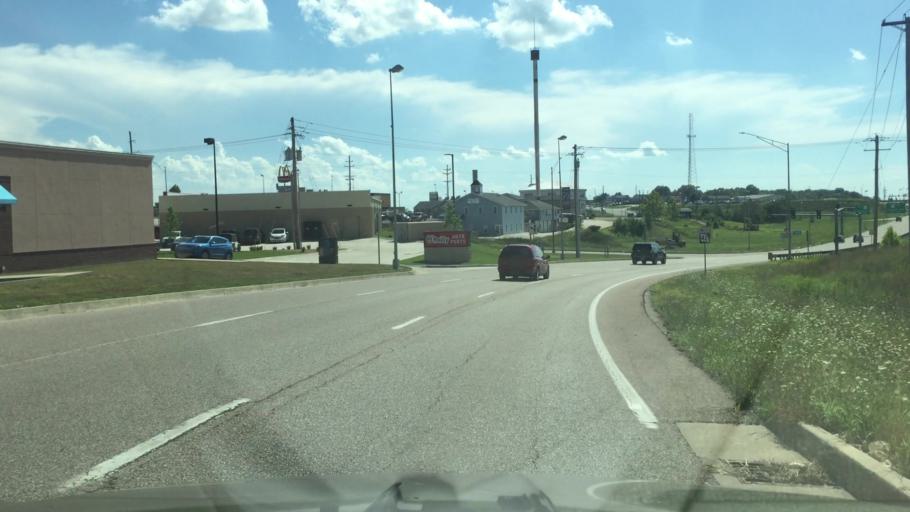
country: US
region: Missouri
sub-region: Miller County
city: Lake Ozark
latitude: 38.1564
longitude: -92.6062
